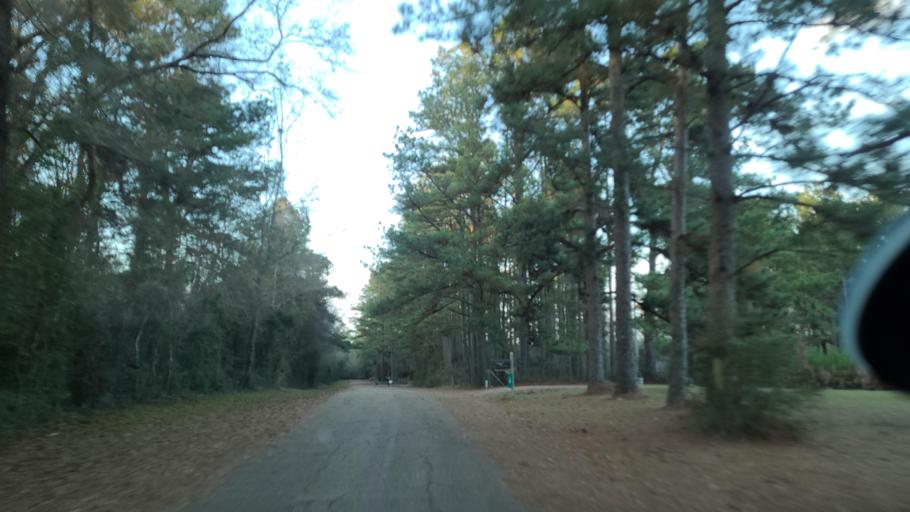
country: US
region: Mississippi
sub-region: Forrest County
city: Hattiesburg
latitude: 31.1804
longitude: -89.2201
